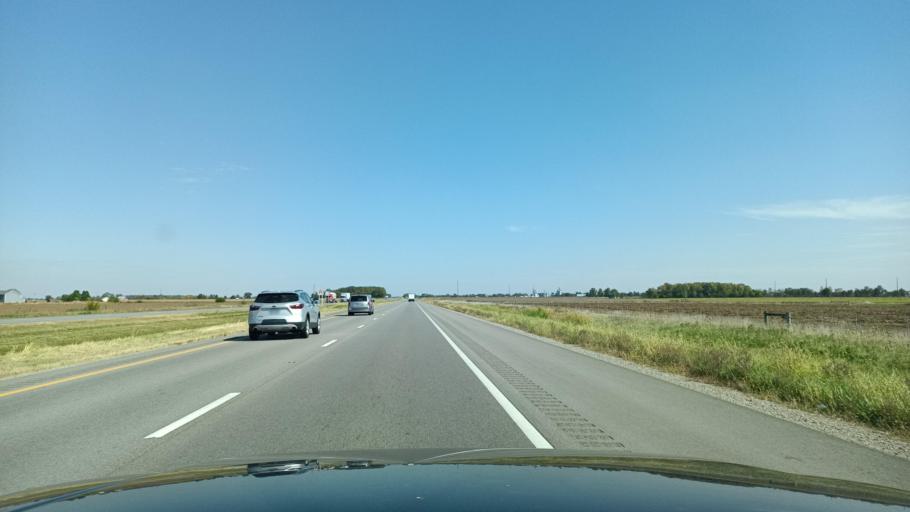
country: US
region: Ohio
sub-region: Defiance County
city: Defiance
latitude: 41.3466
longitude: -84.2500
